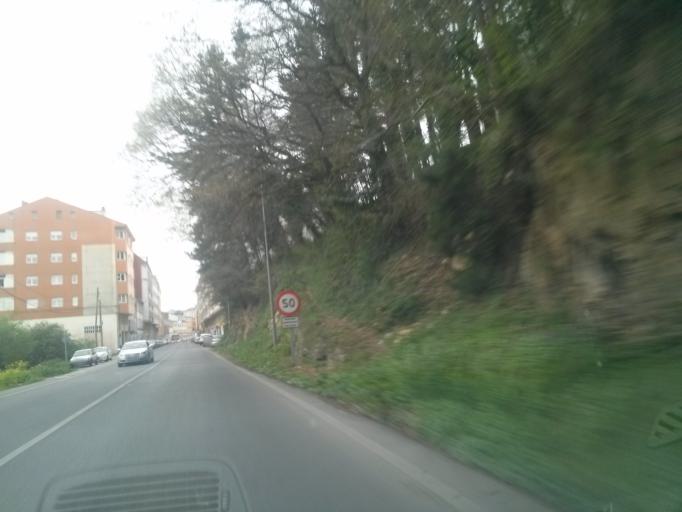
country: ES
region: Galicia
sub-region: Provincia de Lugo
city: Lugo
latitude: 43.0197
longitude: -7.5477
